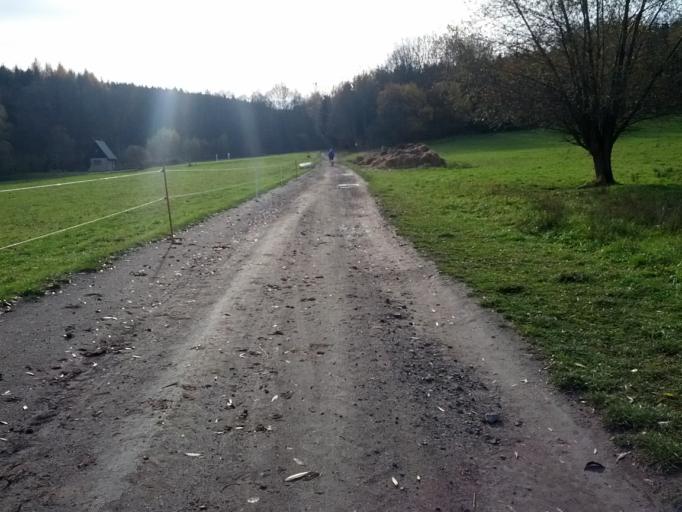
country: DE
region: Thuringia
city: Eisenach
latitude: 50.9590
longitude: 10.3586
